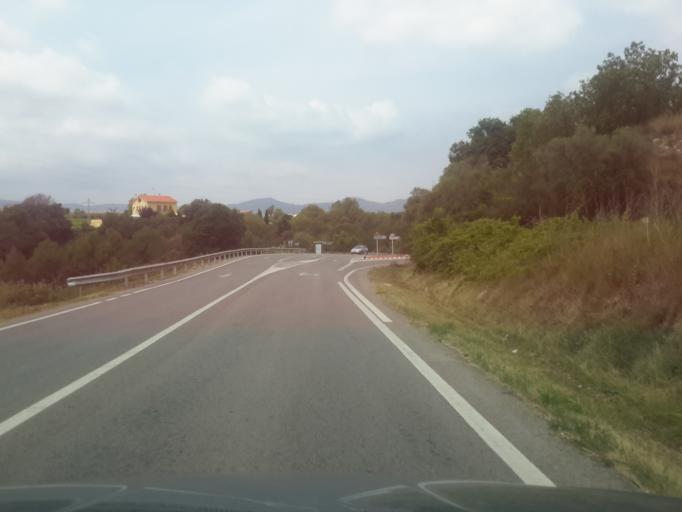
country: ES
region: Catalonia
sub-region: Provincia de Barcelona
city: Vilobi del Penedes
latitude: 41.3819
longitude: 1.6369
